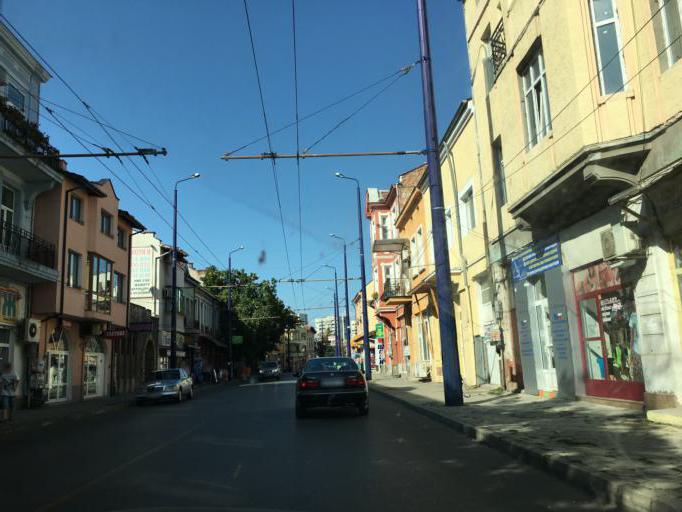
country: BG
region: Pazardzhik
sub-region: Obshtina Pazardzhik
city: Pazardzhik
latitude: 42.1875
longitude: 24.3281
